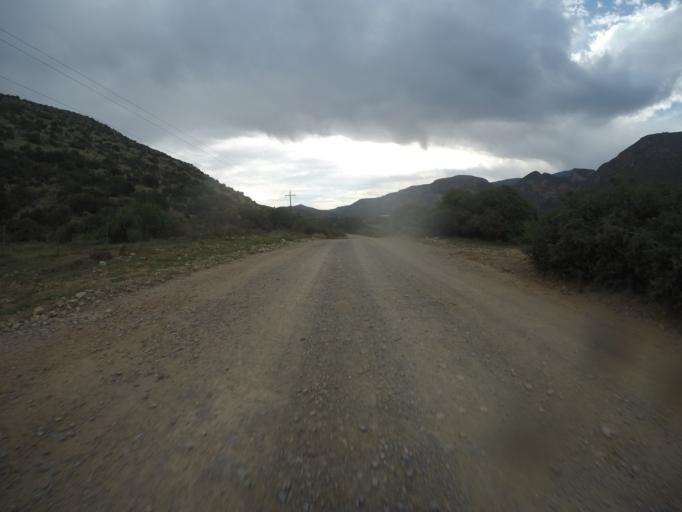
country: ZA
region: Eastern Cape
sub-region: Cacadu District Municipality
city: Willowmore
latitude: -33.5259
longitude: 23.8512
